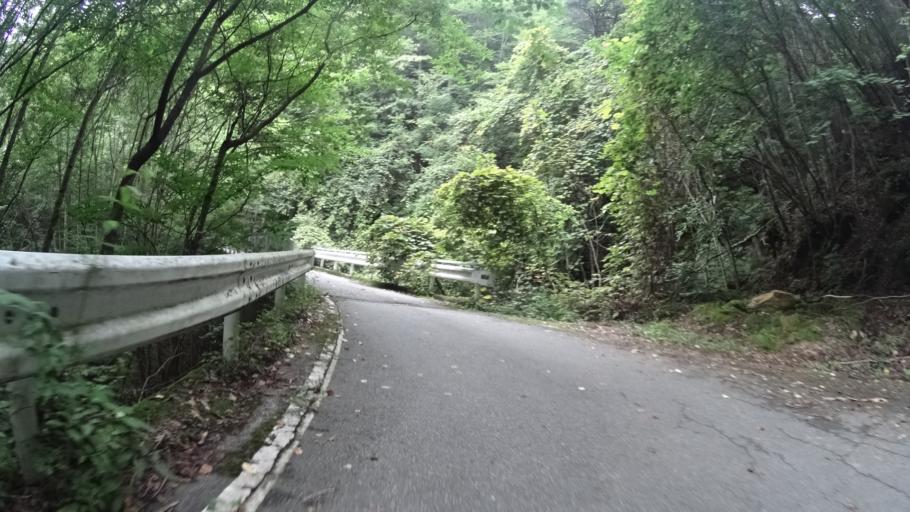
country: JP
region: Yamanashi
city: Kofu-shi
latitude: 35.8081
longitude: 138.6105
